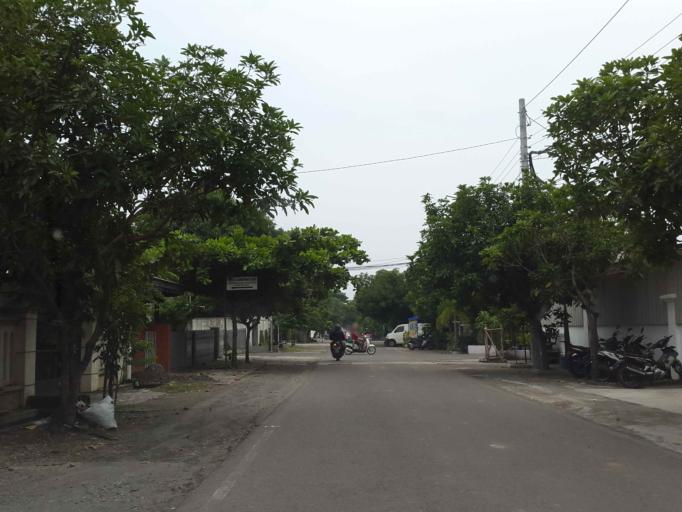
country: ID
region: Central Java
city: Colomadu
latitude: -7.5574
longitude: 110.7865
